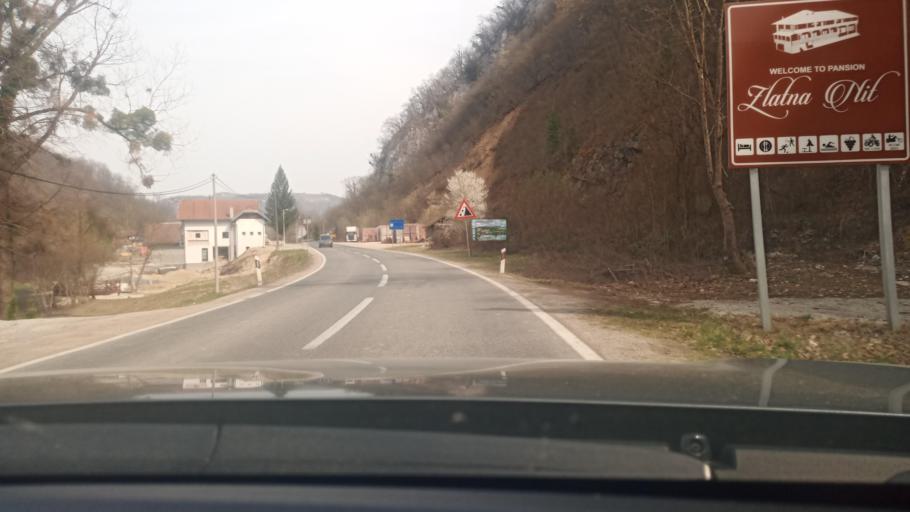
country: BA
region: Federation of Bosnia and Herzegovina
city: Bosanska Krupa
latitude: 44.8775
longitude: 16.1308
